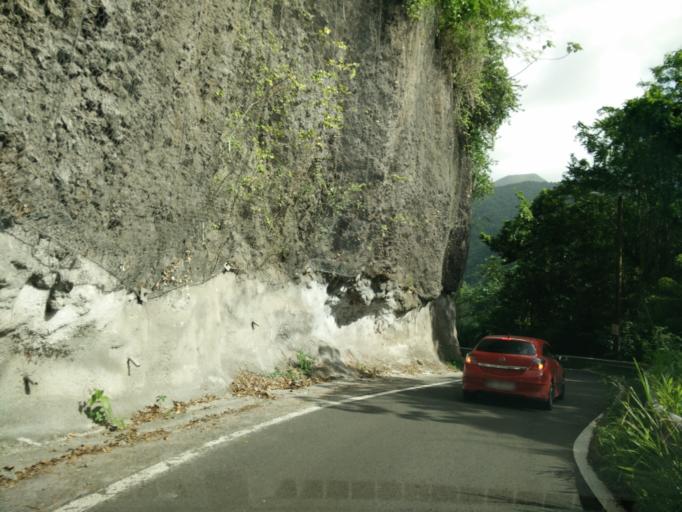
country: MQ
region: Martinique
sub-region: Martinique
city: Basse-Pointe
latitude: 14.8717
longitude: -61.1747
